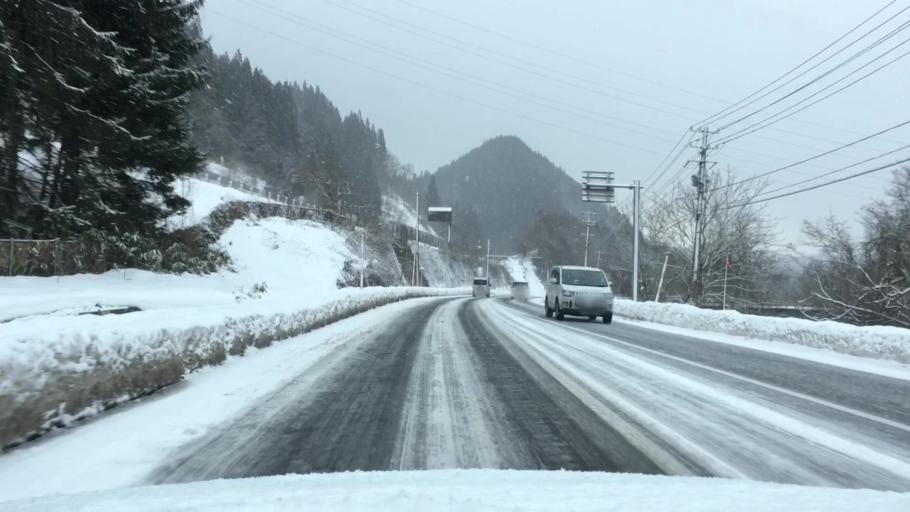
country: JP
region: Aomori
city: Kuroishi
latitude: 40.4622
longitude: 140.6355
